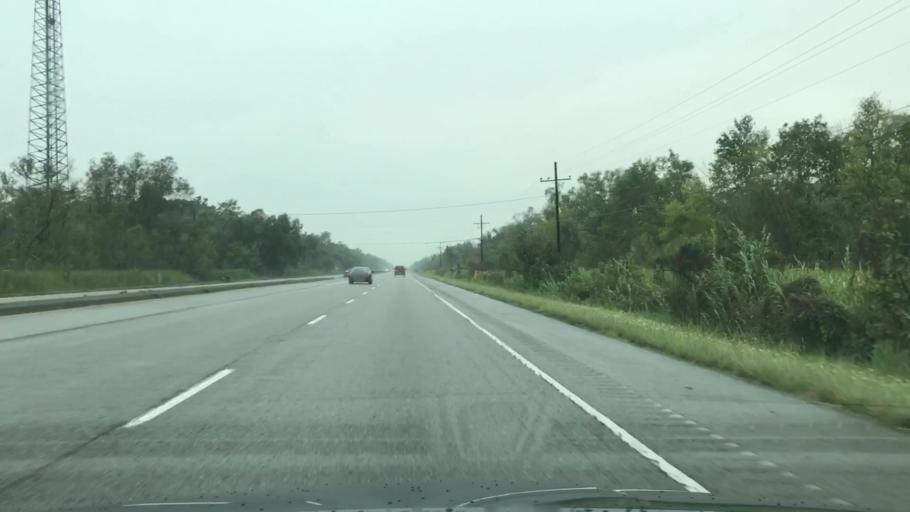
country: US
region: Louisiana
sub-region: Saint Charles Parish
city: Des Allemands
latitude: 29.7838
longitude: -90.5217
